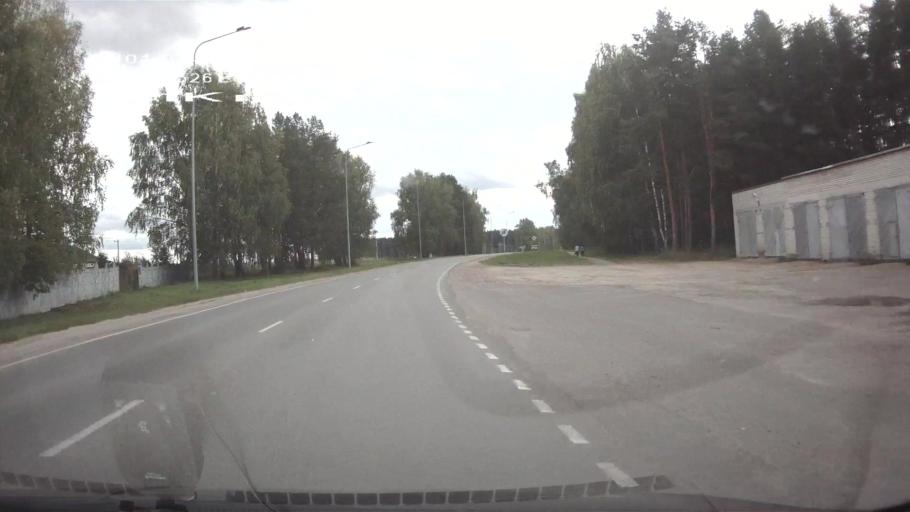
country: RU
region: Mariy-El
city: Kuzhener
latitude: 56.9970
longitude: 48.7419
